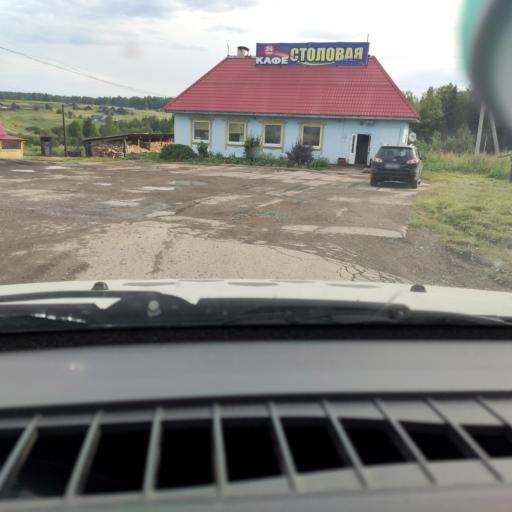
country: RU
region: Perm
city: Siva
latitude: 58.6276
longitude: 53.8709
